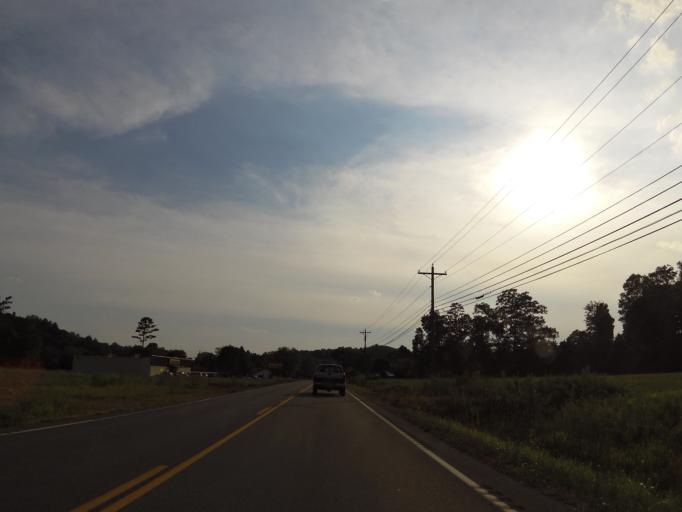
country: US
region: Tennessee
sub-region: Morgan County
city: Coalfield
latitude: 36.0353
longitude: -84.4098
